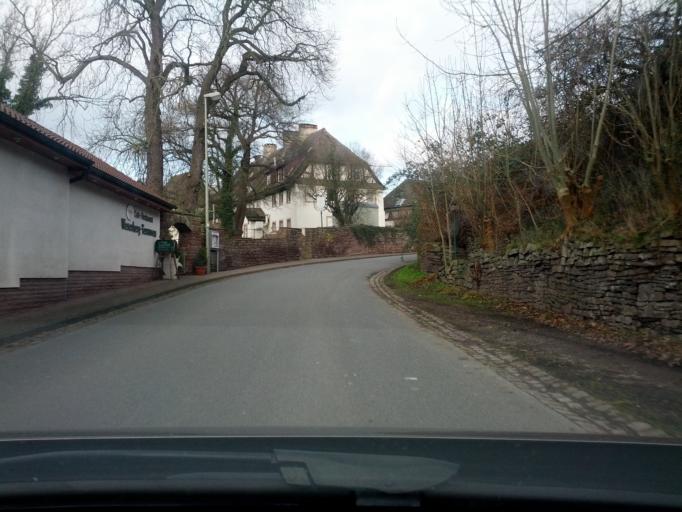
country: DE
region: Lower Saxony
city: Furstenberg
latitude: 51.7301
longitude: 9.3987
